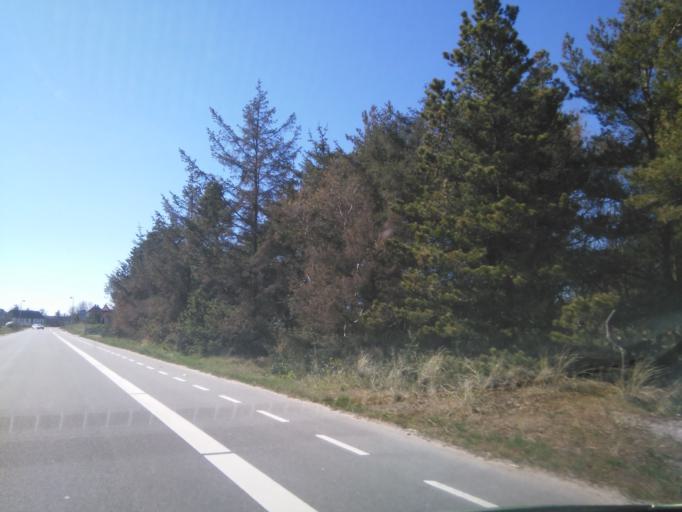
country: DK
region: South Denmark
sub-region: Varde Kommune
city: Oksbol
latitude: 55.5487
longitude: 8.1586
